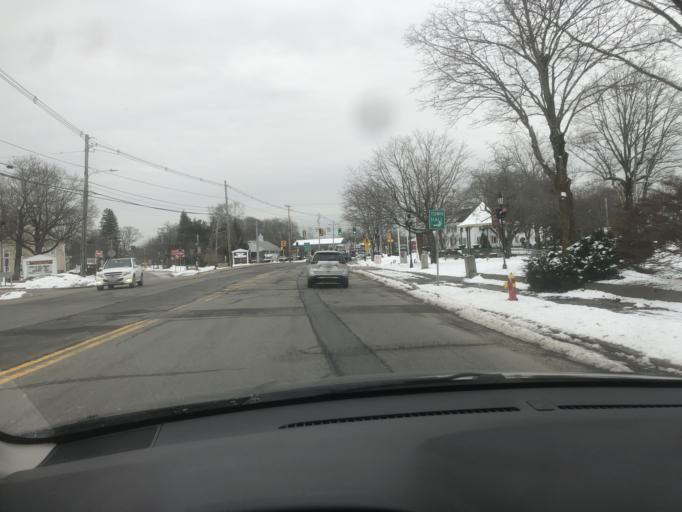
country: US
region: Massachusetts
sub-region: Middlesex County
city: Tewksbury
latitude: 42.6123
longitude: -71.2341
